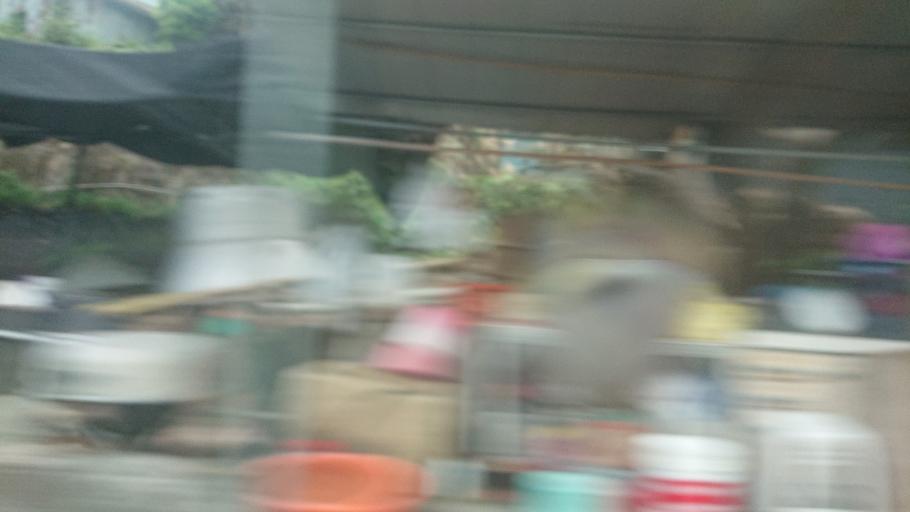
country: TW
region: Taiwan
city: Lugu
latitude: 23.6069
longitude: 120.7085
